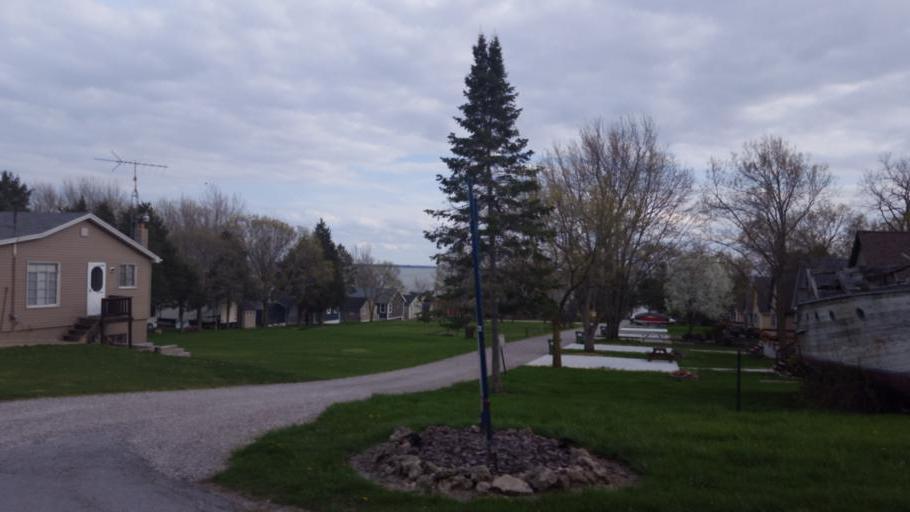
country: US
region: Ohio
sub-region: Erie County
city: Sandusky
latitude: 41.5053
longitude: -82.7638
